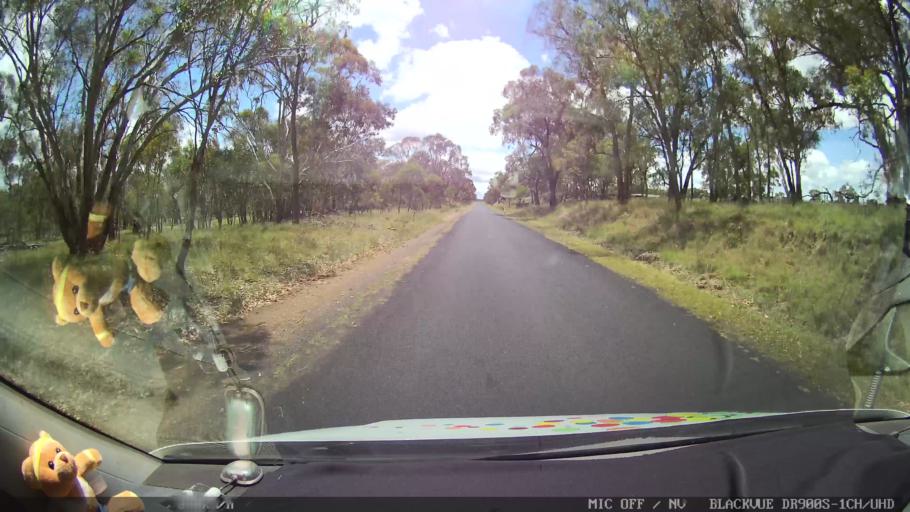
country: AU
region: New South Wales
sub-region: Glen Innes Severn
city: Glen Innes
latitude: -29.4319
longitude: 151.6879
